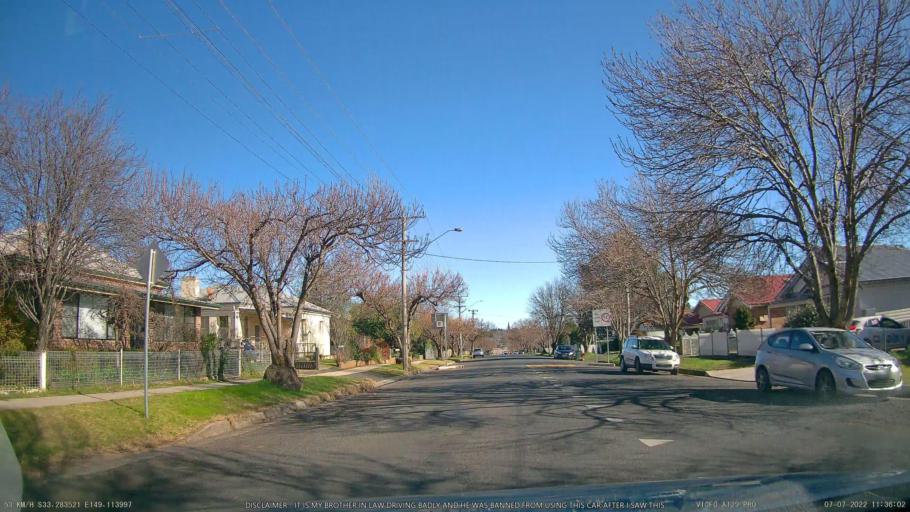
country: AU
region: New South Wales
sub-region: Orange Municipality
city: Orange
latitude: -33.2834
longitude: 149.1135
